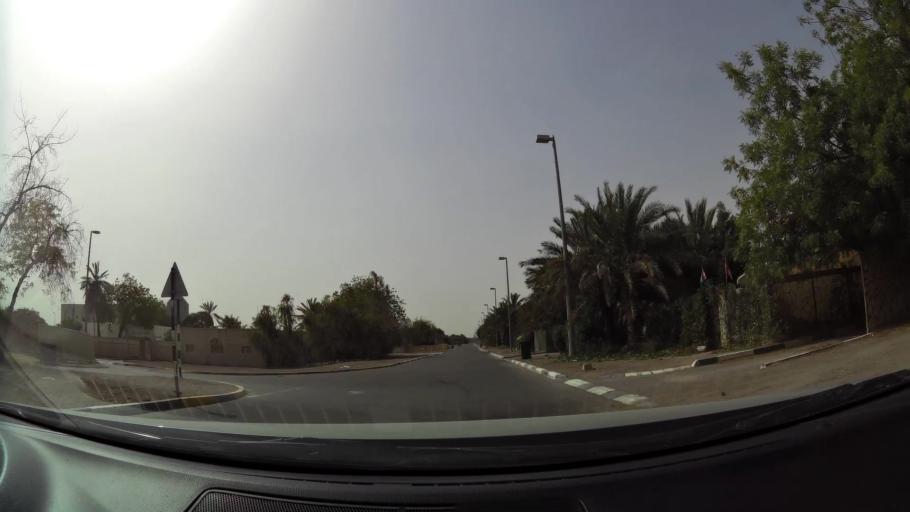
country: AE
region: Abu Dhabi
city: Al Ain
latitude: 24.1825
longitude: 55.6211
